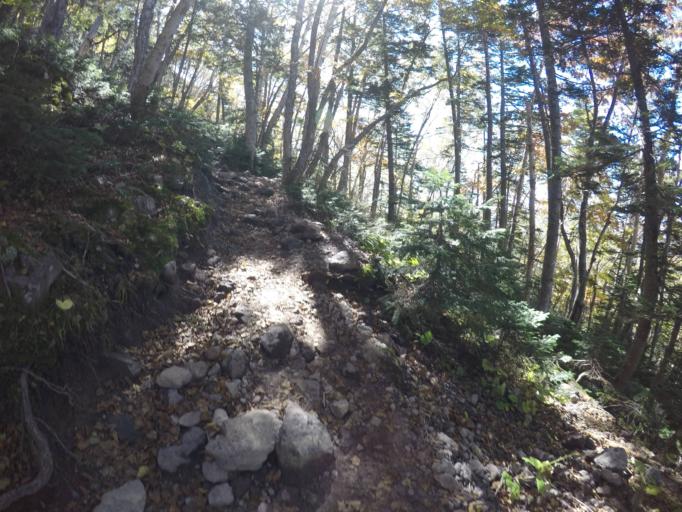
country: JP
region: Tochigi
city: Nikko
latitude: 36.7985
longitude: 139.3689
